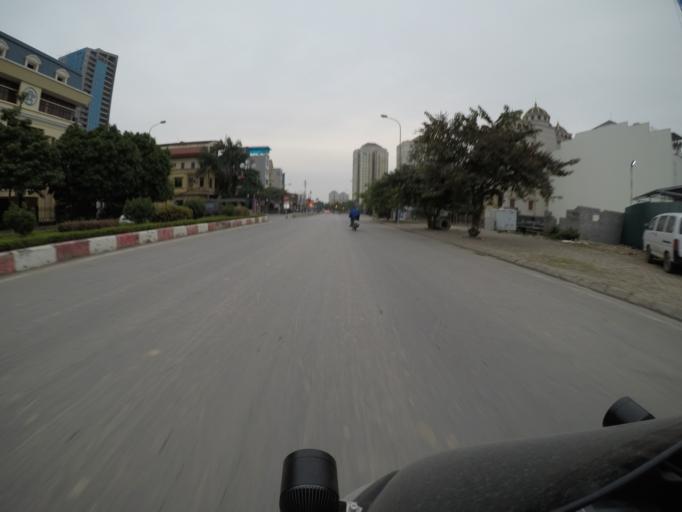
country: VN
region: Ha Noi
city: Tay Ho
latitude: 21.0698
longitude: 105.8110
